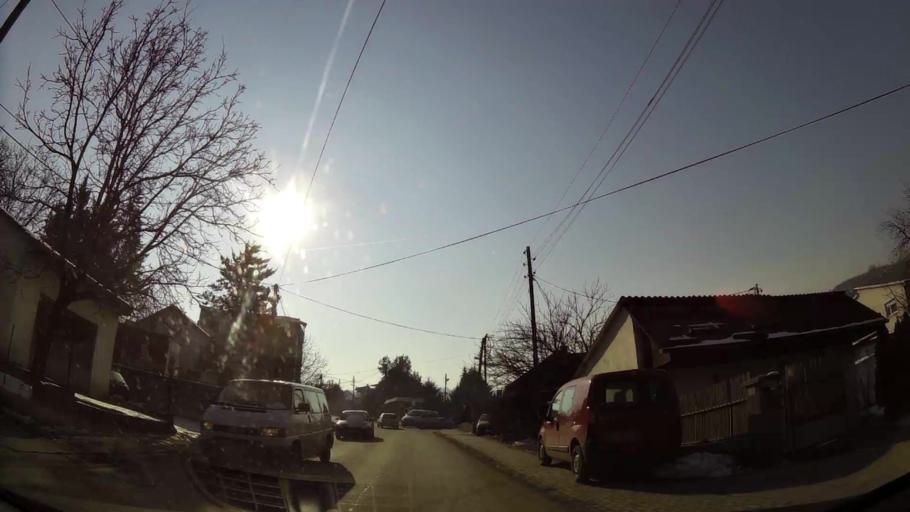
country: MK
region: Kisela Voda
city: Usje
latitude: 41.9674
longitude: 21.4487
